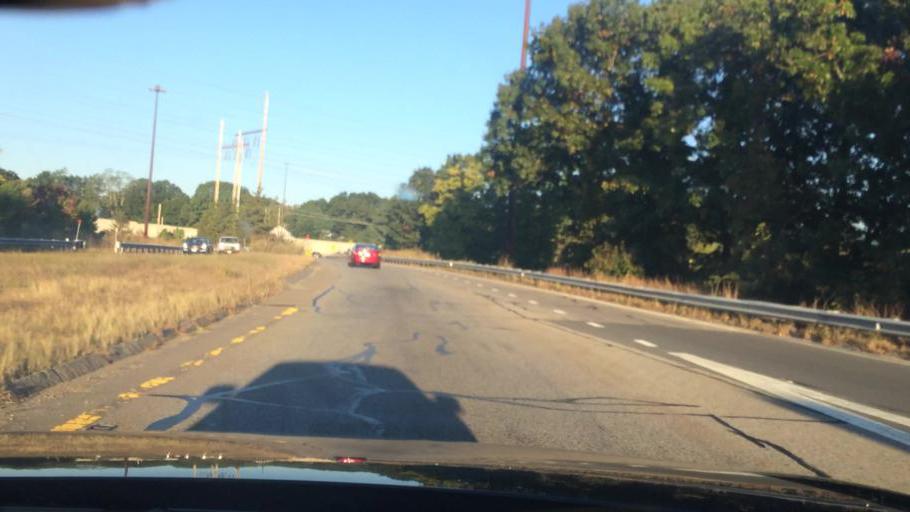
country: US
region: Massachusetts
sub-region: Middlesex County
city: Lowell
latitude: 42.6087
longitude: -71.3238
